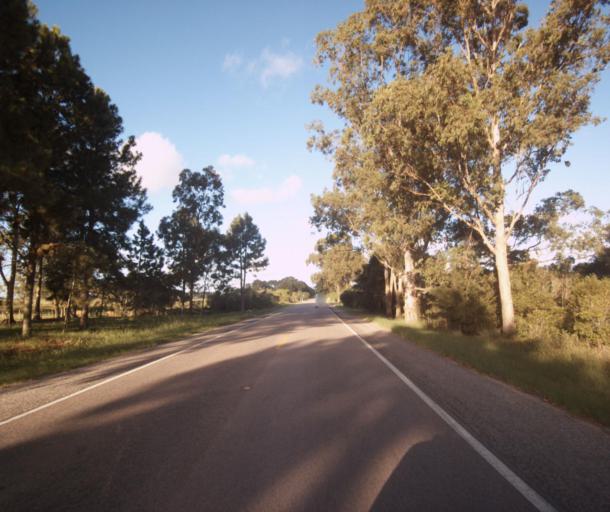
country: BR
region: Rio Grande do Sul
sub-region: Rio Grande
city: Rio Grande
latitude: -32.0963
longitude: -52.3168
